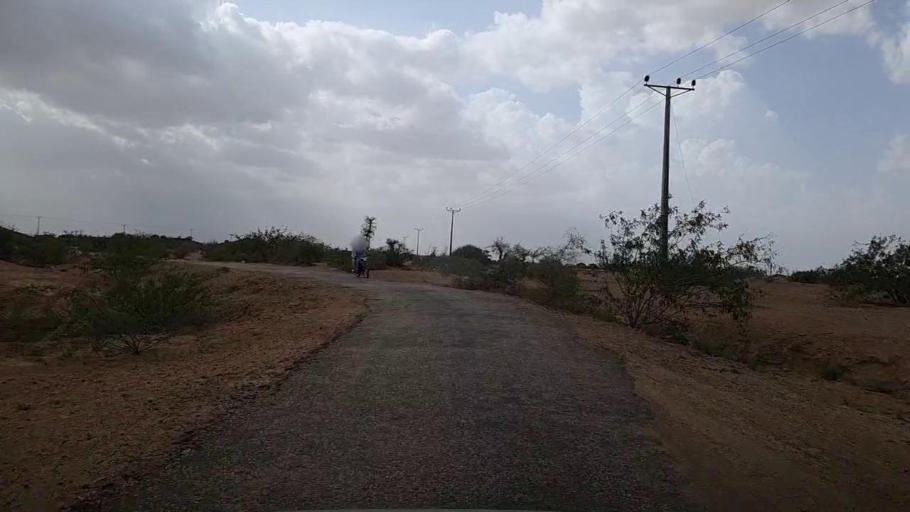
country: PK
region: Sindh
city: Jamshoro
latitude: 25.4006
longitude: 67.7138
